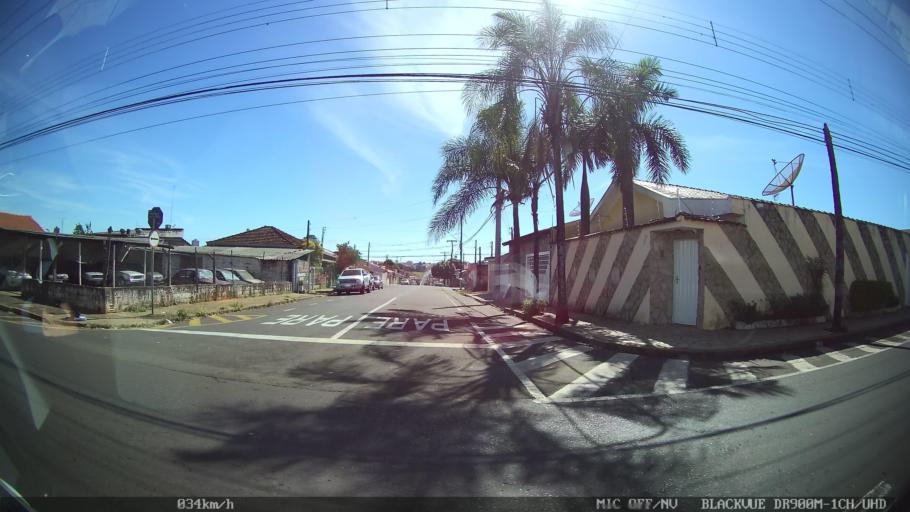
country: BR
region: Sao Paulo
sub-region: Franca
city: Franca
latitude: -20.5421
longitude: -47.3829
